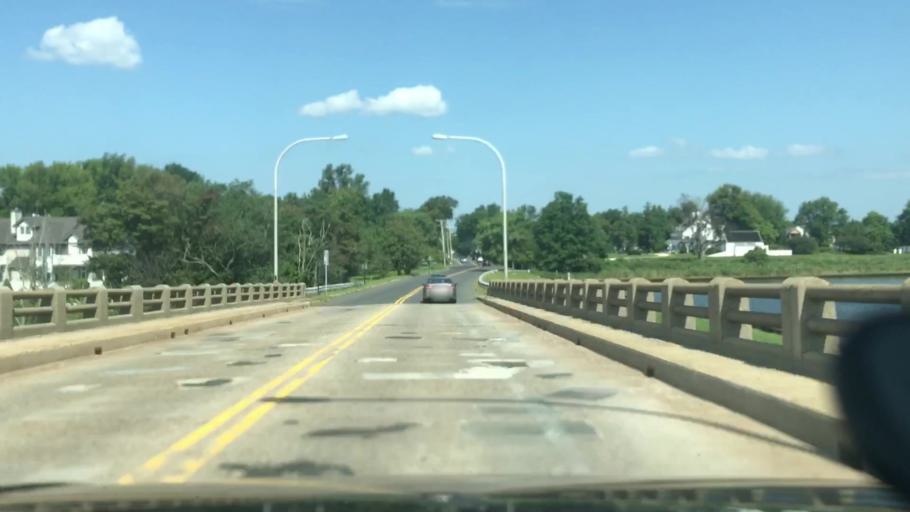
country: US
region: New Jersey
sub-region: Monmouth County
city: Oceanport
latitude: 40.3262
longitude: -74.0207
